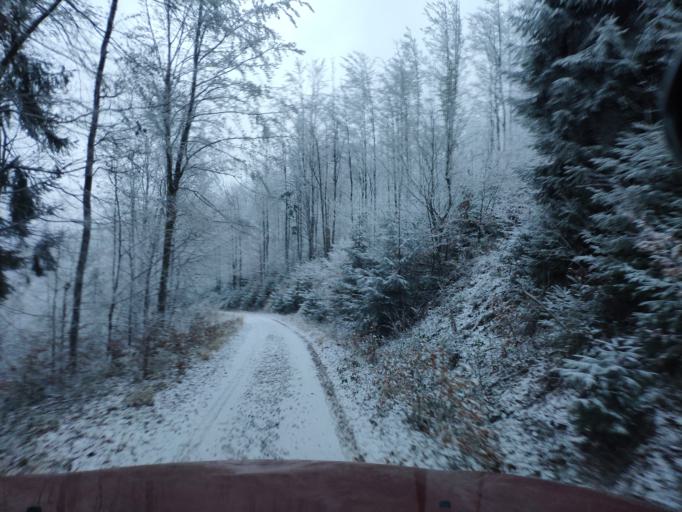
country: SK
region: Kosicky
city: Dobsina
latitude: 48.8103
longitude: 20.4911
